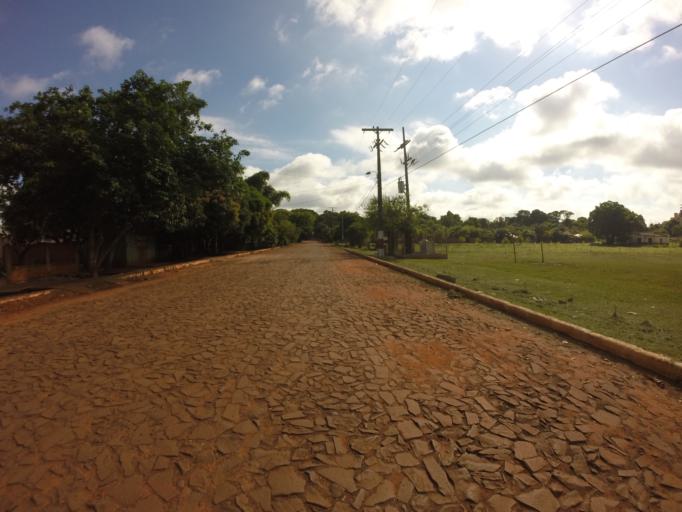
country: PY
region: Alto Parana
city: Ciudad del Este
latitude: -25.3954
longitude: -54.6436
